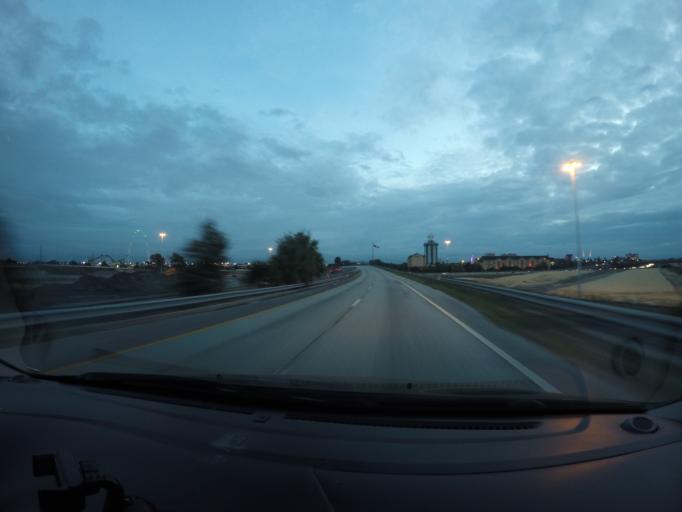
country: US
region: Florida
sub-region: Orange County
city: Tangelo Park
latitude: 28.4692
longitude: -81.4607
